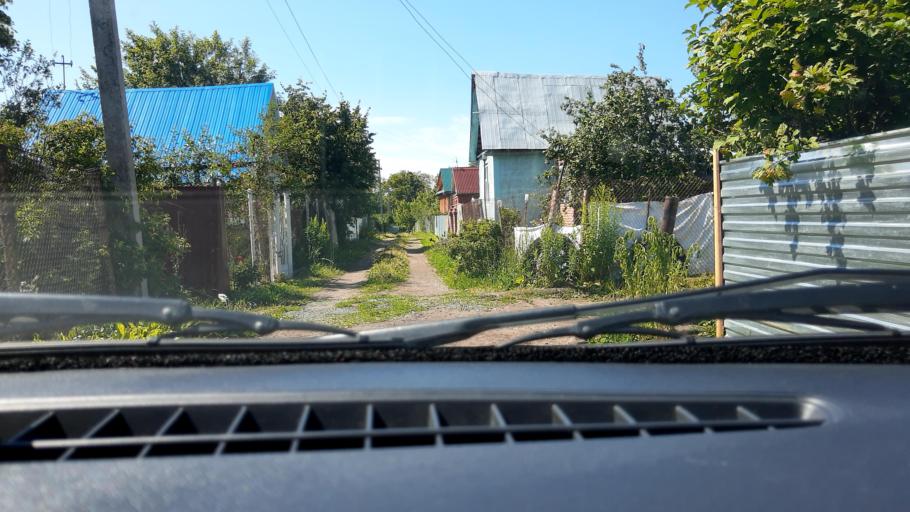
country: RU
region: Bashkortostan
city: Karmaskaly
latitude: 54.3622
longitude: 55.8895
